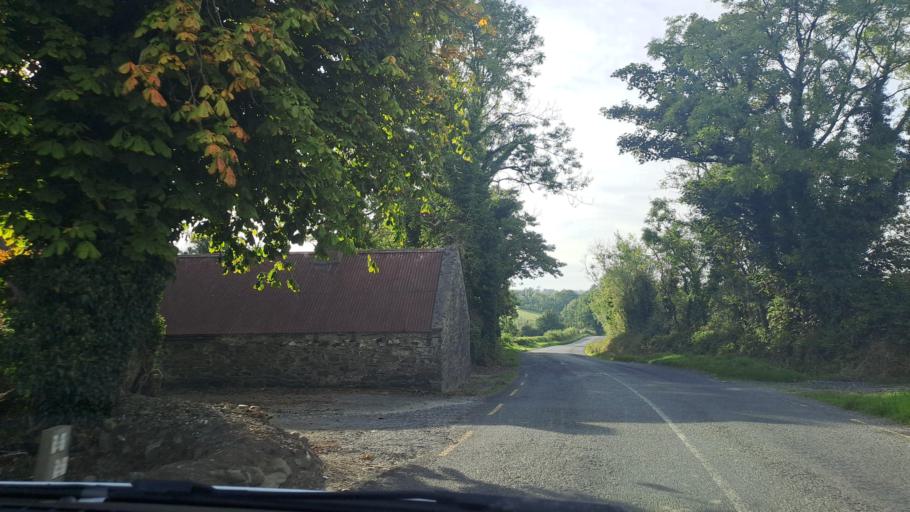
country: IE
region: Ulster
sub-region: An Cabhan
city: Kingscourt
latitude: 53.9543
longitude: -6.8436
